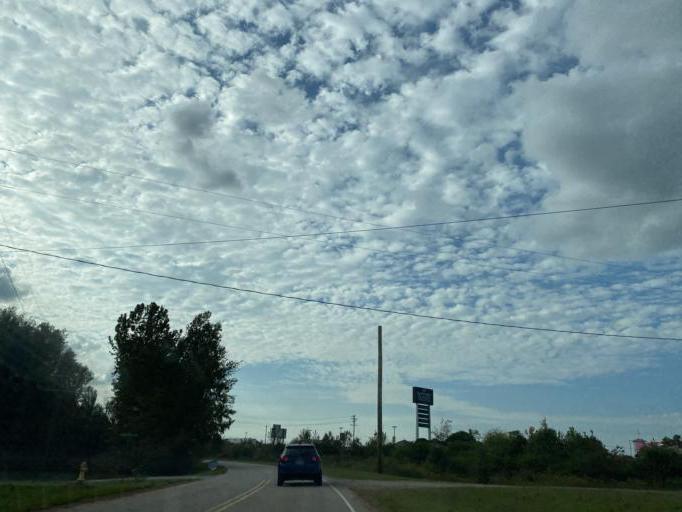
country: US
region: South Carolina
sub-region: Cherokee County
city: Gaffney
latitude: 35.0810
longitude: -81.7072
